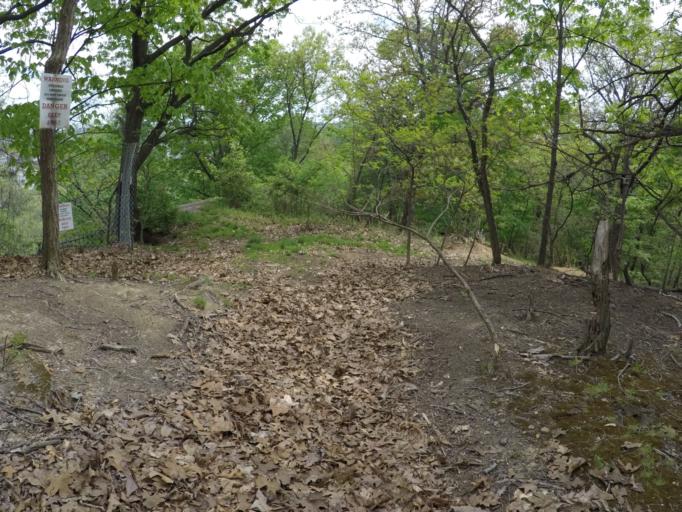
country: US
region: West Virginia
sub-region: Cabell County
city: Huntington
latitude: 38.4159
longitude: -82.3915
